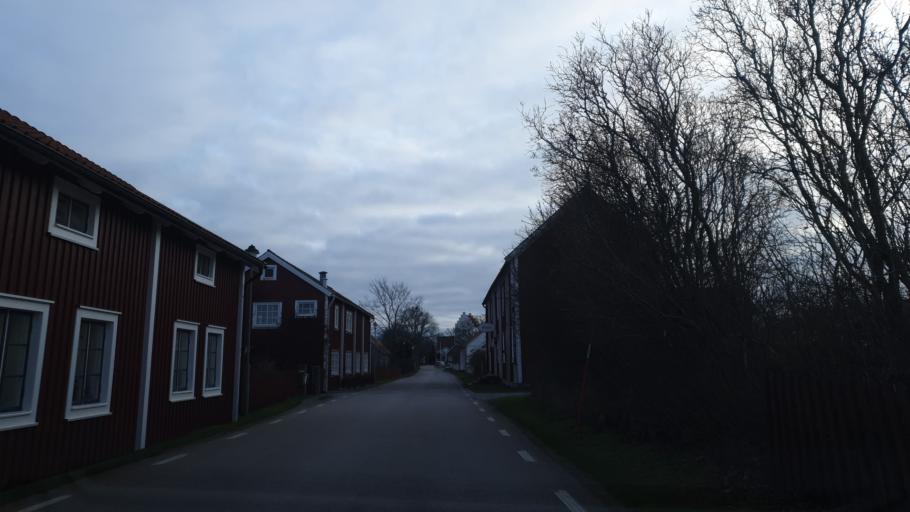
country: SE
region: Kalmar
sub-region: Torsas Kommun
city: Torsas
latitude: 56.2595
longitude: 16.0410
